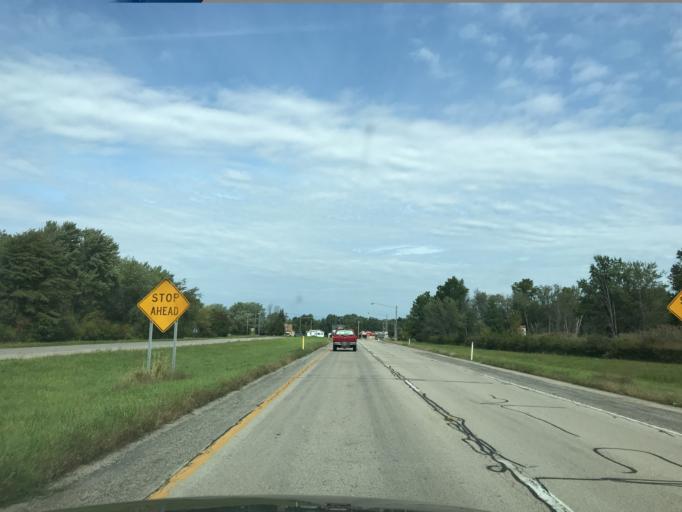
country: US
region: Ohio
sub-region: Ashtabula County
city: Edgewood
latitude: 41.8980
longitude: -80.7819
